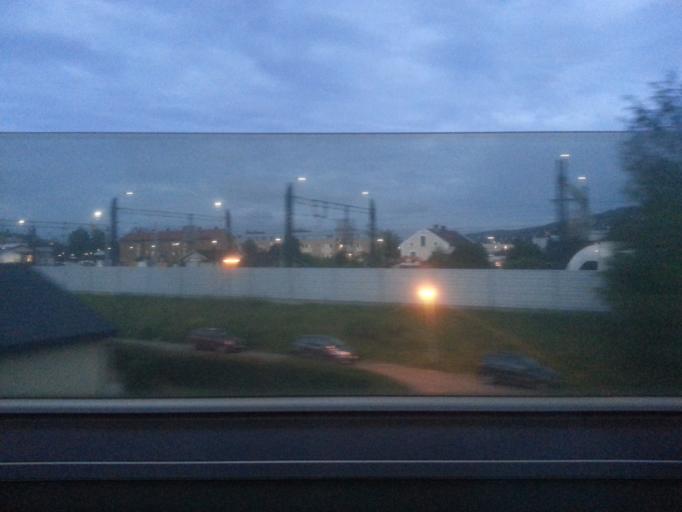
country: NO
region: Akershus
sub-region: Skedsmo
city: Lillestrom
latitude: 59.9545
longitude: 11.0514
